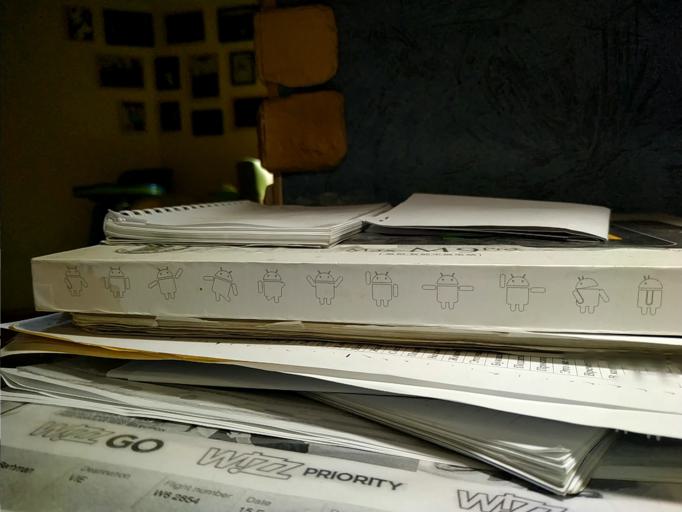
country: RU
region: Novgorod
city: Poddor'ye
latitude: 57.5206
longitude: 30.9173
